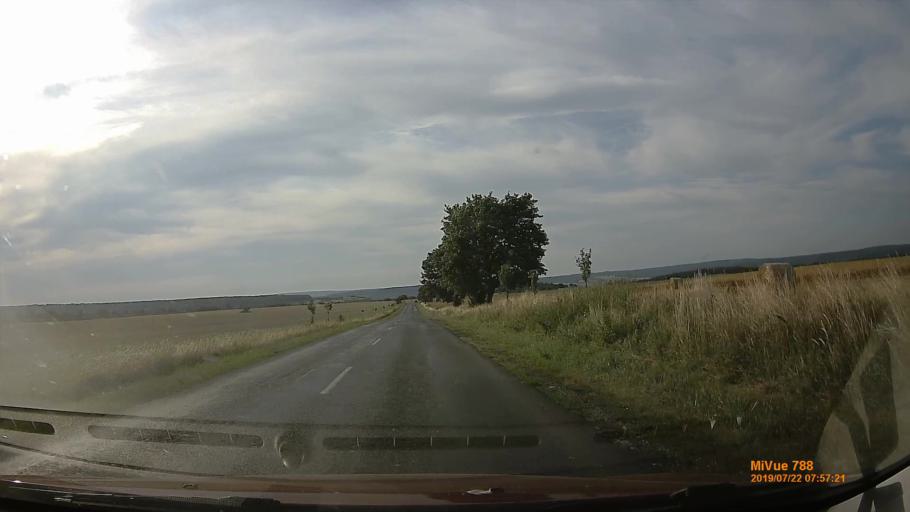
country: HU
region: Veszprem
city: Ajka
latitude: 47.0179
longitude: 17.5824
